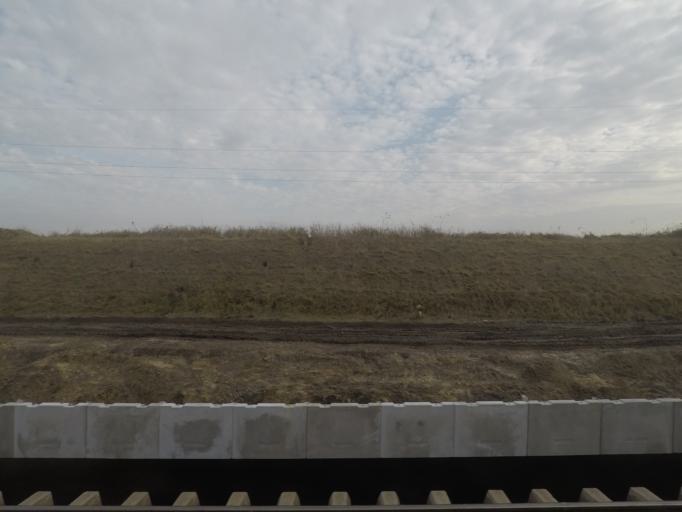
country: PL
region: Subcarpathian Voivodeship
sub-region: Powiat jaroslawski
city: Sosnica
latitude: 49.8623
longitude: 22.8570
